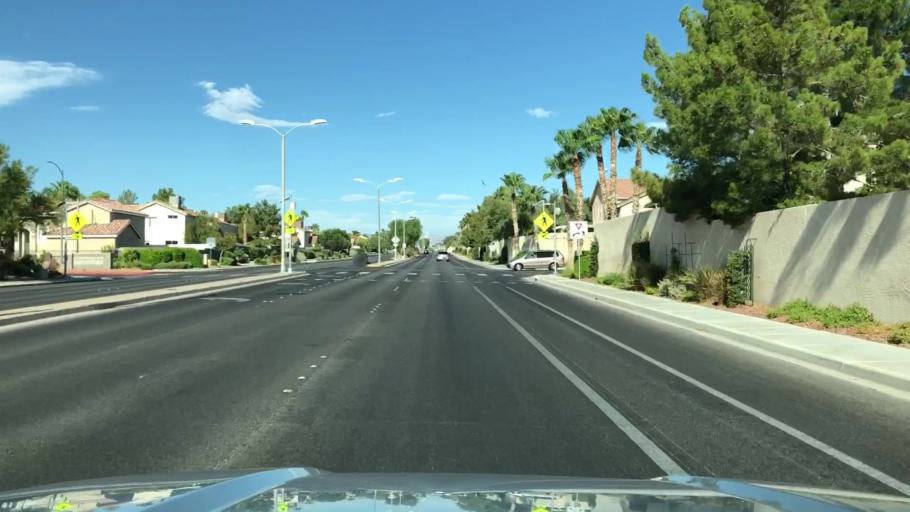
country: US
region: Nevada
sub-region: Clark County
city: Whitney
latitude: 36.0423
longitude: -115.0916
